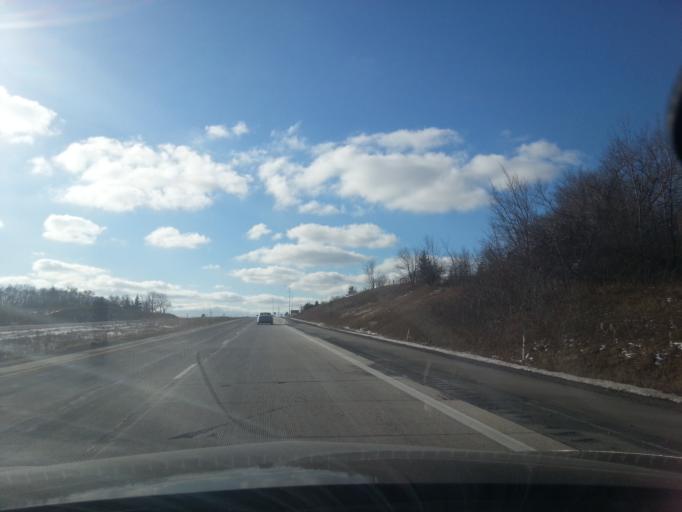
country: CA
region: Ontario
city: Omemee
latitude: 44.1582
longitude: -78.4891
